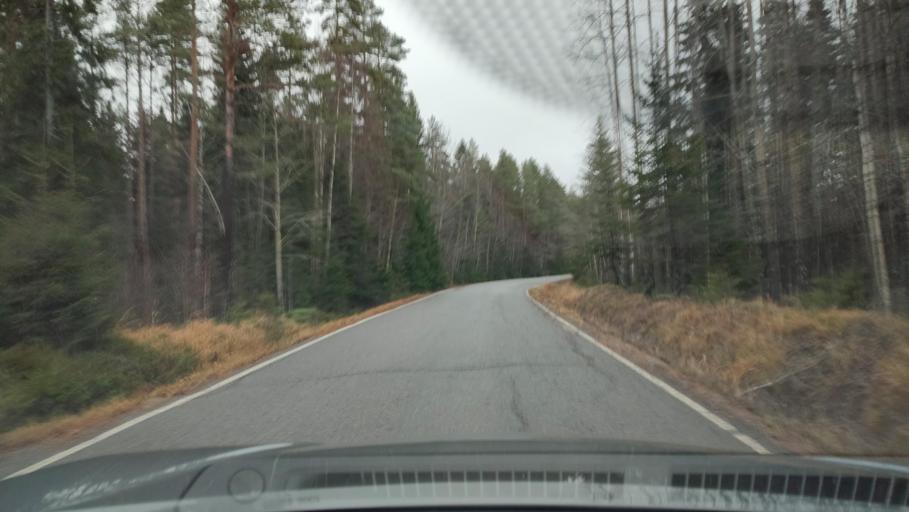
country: FI
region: Southern Ostrobothnia
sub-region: Suupohja
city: Isojoki
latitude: 62.1642
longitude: 21.8902
